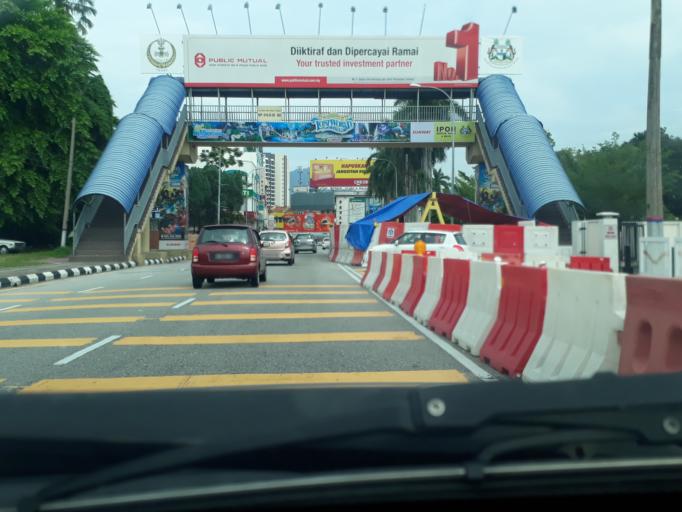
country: MY
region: Perak
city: Ipoh
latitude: 4.5919
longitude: 101.0879
